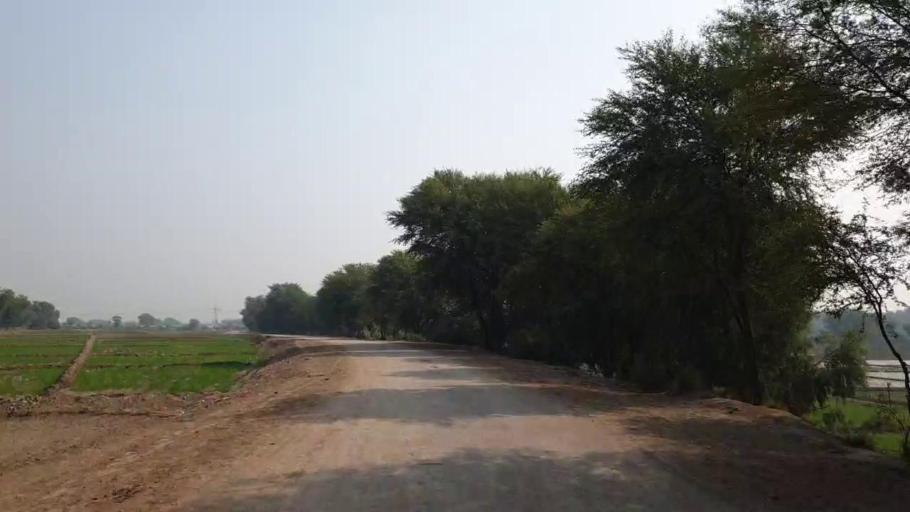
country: PK
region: Sindh
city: Bhan
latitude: 26.5169
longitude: 67.7389
